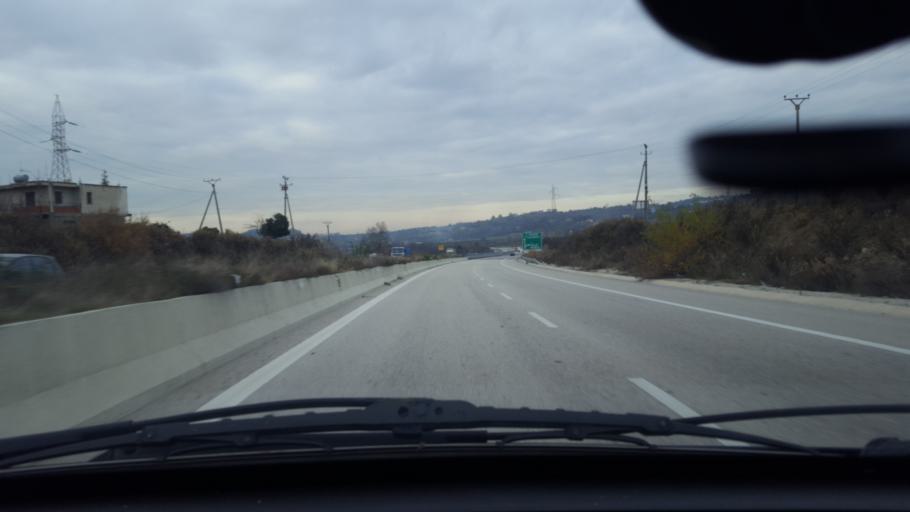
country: AL
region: Tirane
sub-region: Rrethi i Tiranes
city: Berzhite
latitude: 41.2529
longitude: 19.8944
